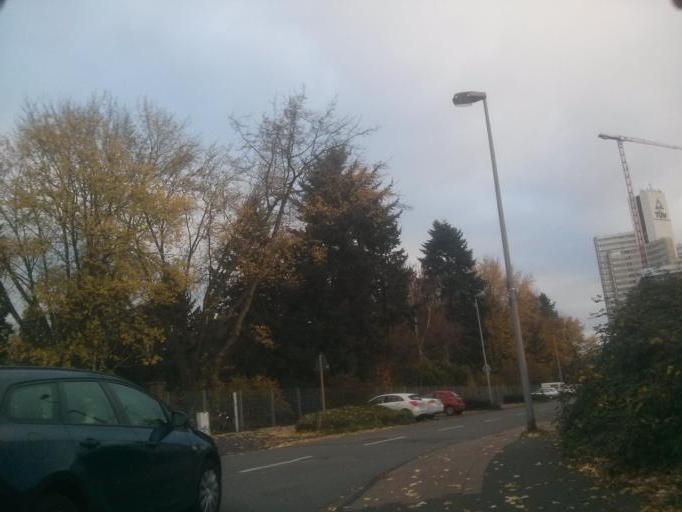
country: DE
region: North Rhine-Westphalia
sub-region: Regierungsbezirk Koln
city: Poll
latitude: 50.9211
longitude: 6.9896
